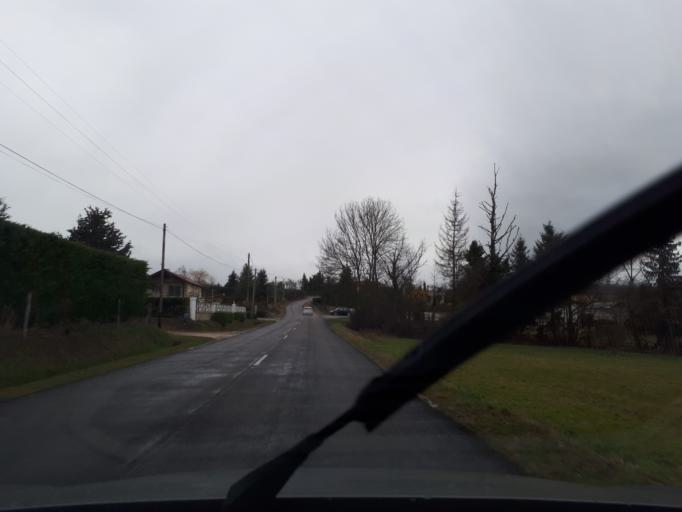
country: FR
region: Rhone-Alpes
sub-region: Departement de la Loire
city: Boen-sur-Lignon
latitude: 45.7712
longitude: 3.9987
